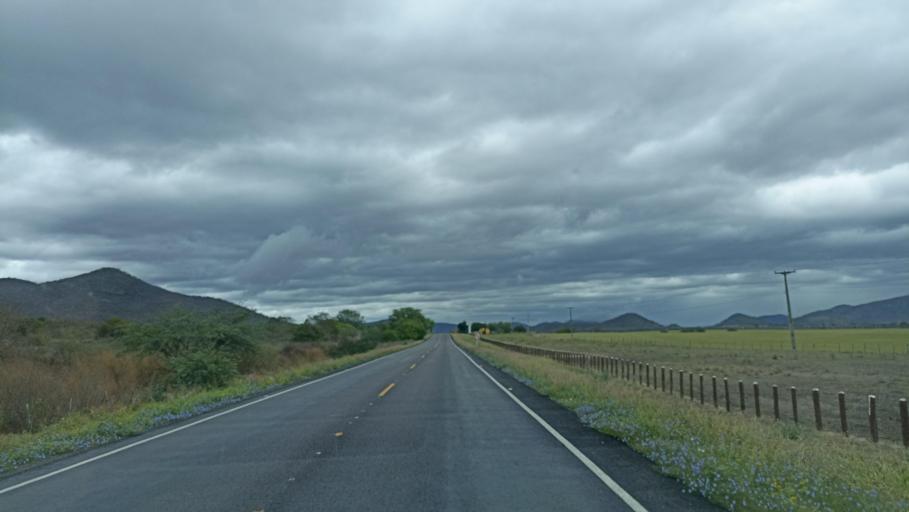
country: BR
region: Bahia
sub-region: Iacu
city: Iacu
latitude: -12.8876
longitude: -40.3945
